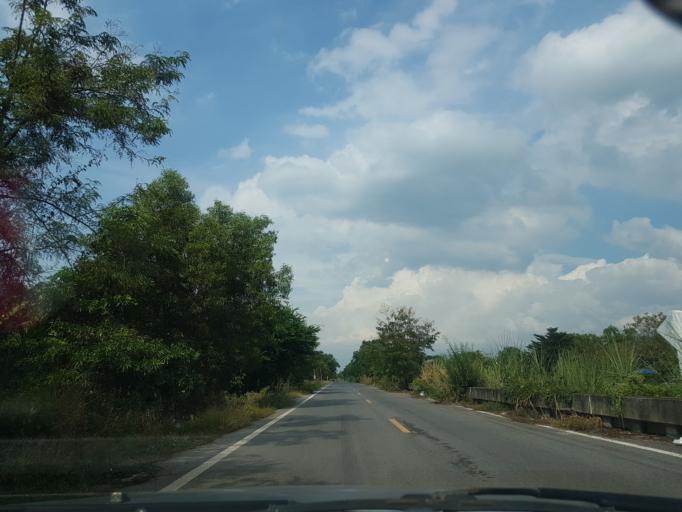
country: TH
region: Sara Buri
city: Nong Khae
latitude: 14.2285
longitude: 100.8914
